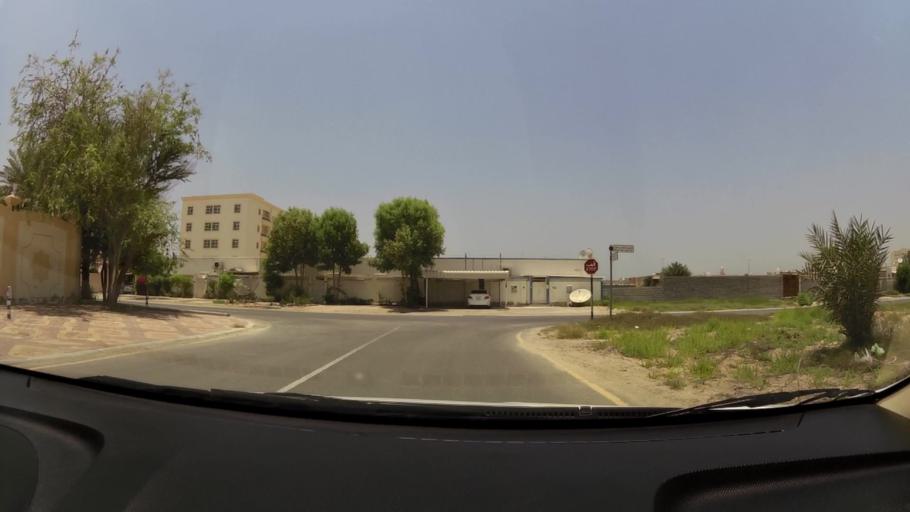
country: AE
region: Umm al Qaywayn
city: Umm al Qaywayn
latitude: 25.5364
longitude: 55.5407
